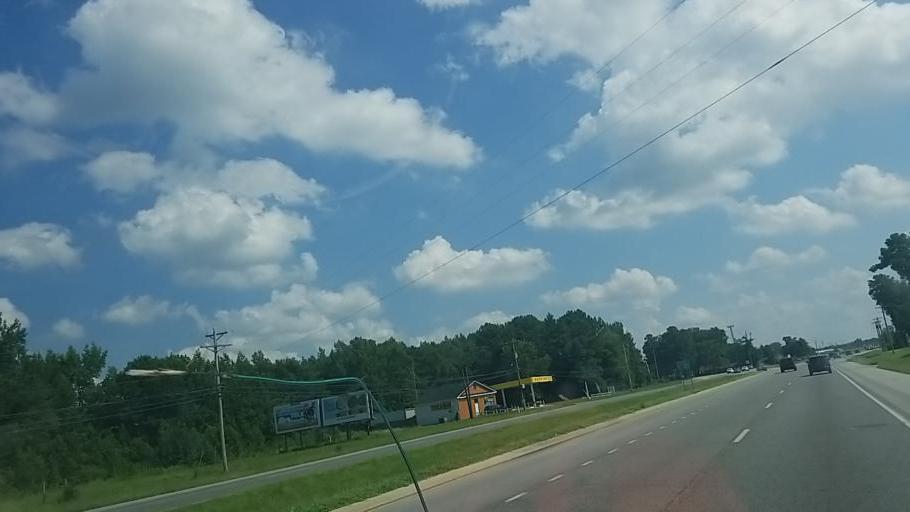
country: US
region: Delaware
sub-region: Sussex County
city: Georgetown
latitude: 38.7080
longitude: -75.4040
